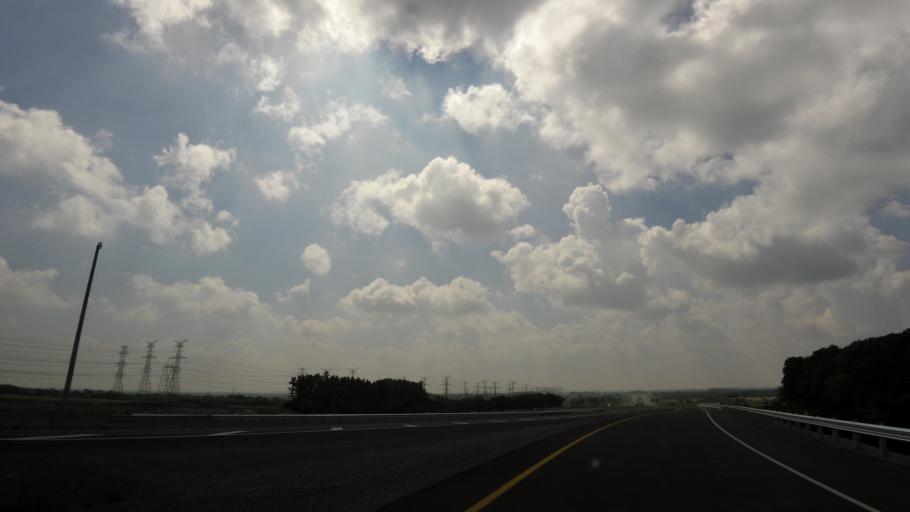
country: CA
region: Ontario
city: Oshawa
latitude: 43.9824
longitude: -78.8706
